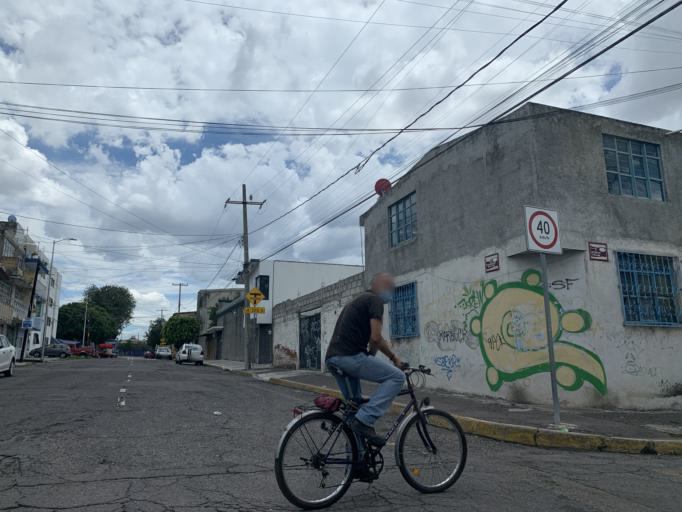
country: MX
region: Puebla
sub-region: Cuautlancingo
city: Sanctorum
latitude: 19.0750
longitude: -98.2350
